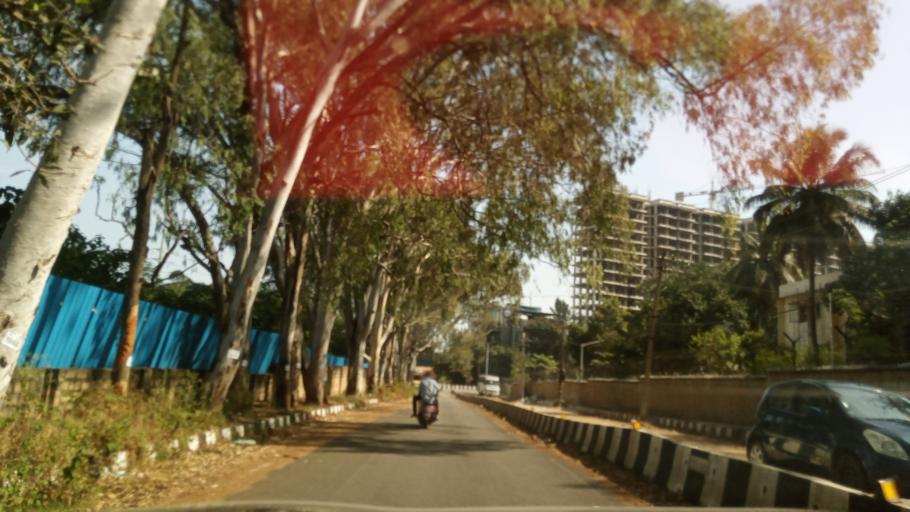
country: IN
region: Karnataka
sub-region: Bangalore Urban
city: Bangalore
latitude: 13.0333
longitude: 77.5396
